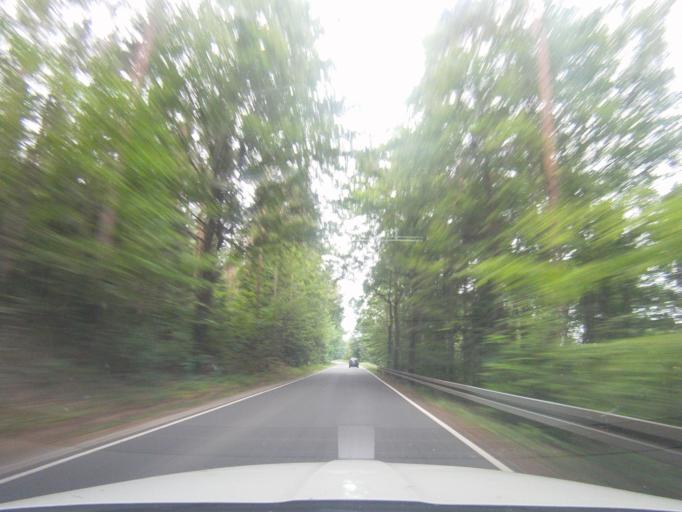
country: DE
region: Thuringia
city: Sankt Kilian
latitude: 50.5017
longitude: 10.8291
